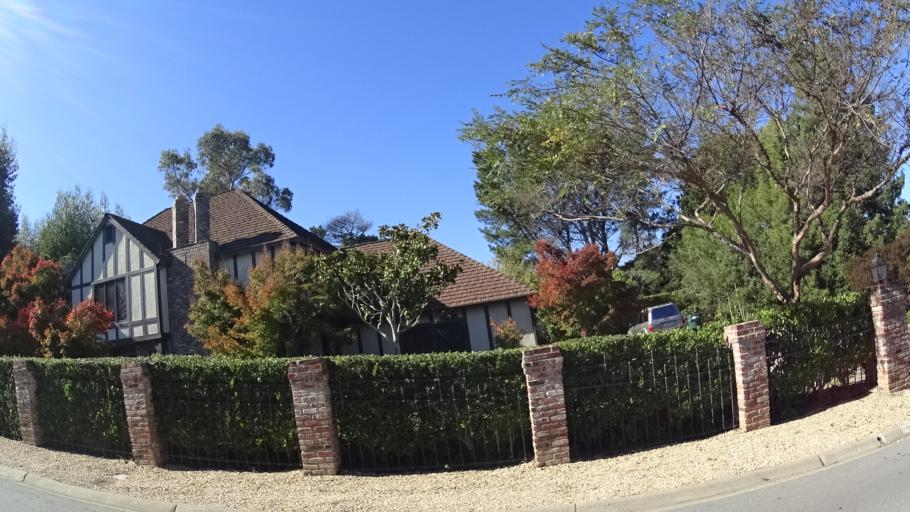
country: US
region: California
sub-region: San Mateo County
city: Hillsborough
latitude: 37.5649
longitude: -122.3756
